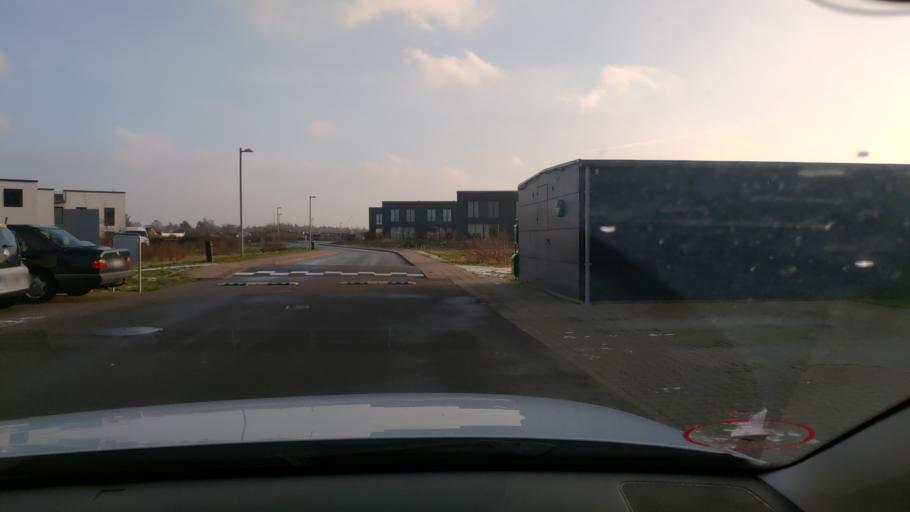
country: DK
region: Zealand
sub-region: Solrod Kommune
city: Solrod Strand
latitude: 55.5464
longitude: 12.2264
